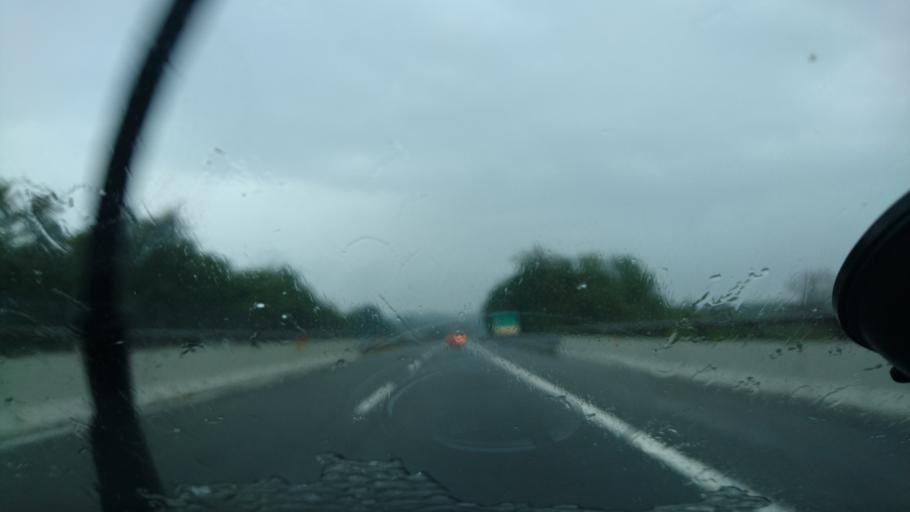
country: IT
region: Piedmont
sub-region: Provincia di Novara
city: Cressa
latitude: 45.6591
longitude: 8.4939
